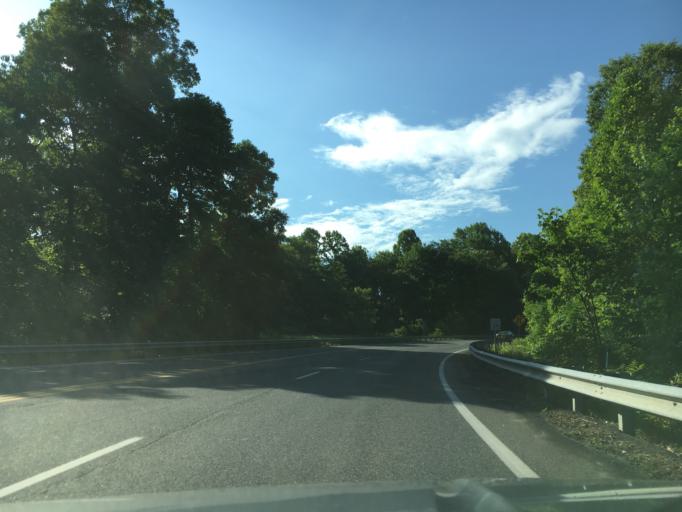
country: US
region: Virginia
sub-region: Campbell County
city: Timberlake
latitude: 37.3468
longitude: -79.2415
